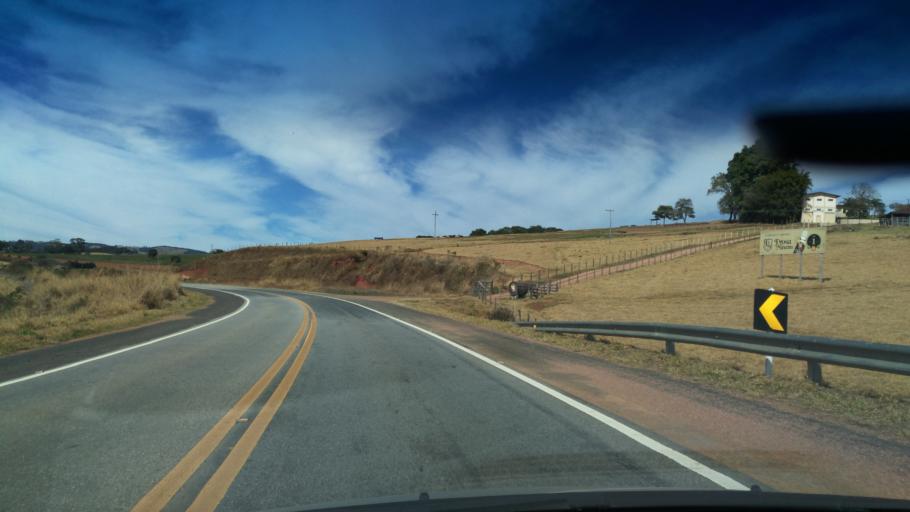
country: BR
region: Minas Gerais
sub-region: Borda Da Mata
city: Borda da Mata
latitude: -22.0541
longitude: -46.2888
